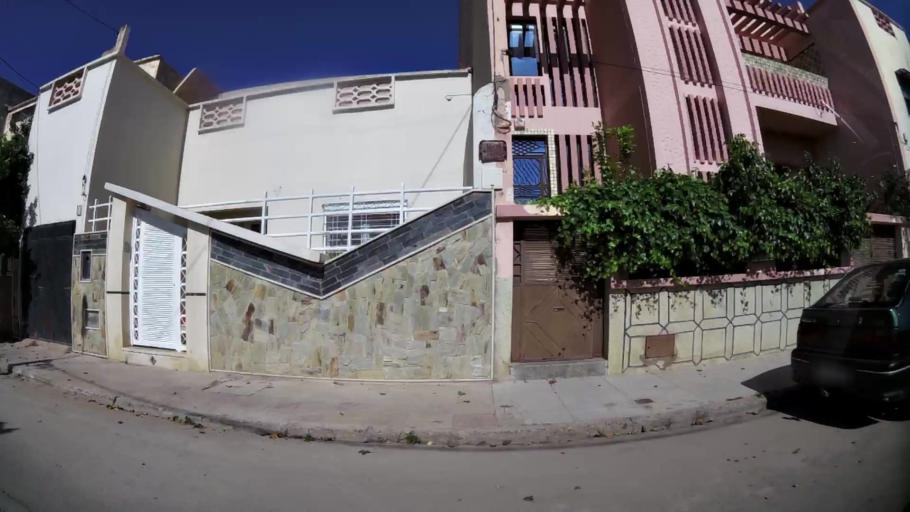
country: MA
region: Oriental
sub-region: Oujda-Angad
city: Oujda
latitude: 34.6889
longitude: -1.9227
